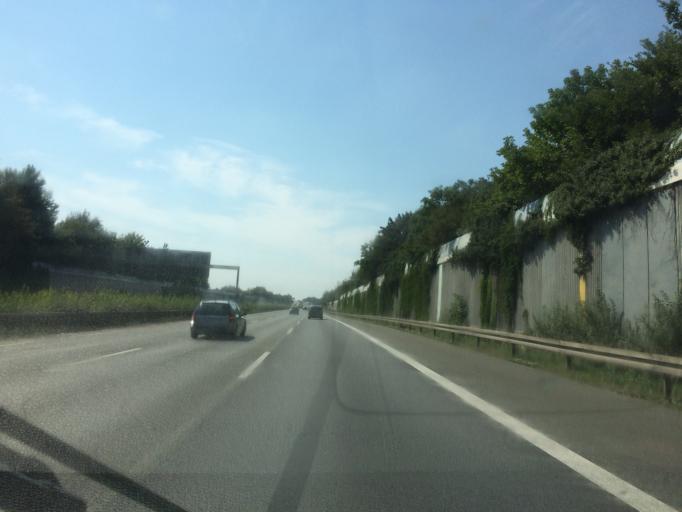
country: DE
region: North Rhine-Westphalia
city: Kamen
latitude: 51.6006
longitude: 7.6599
